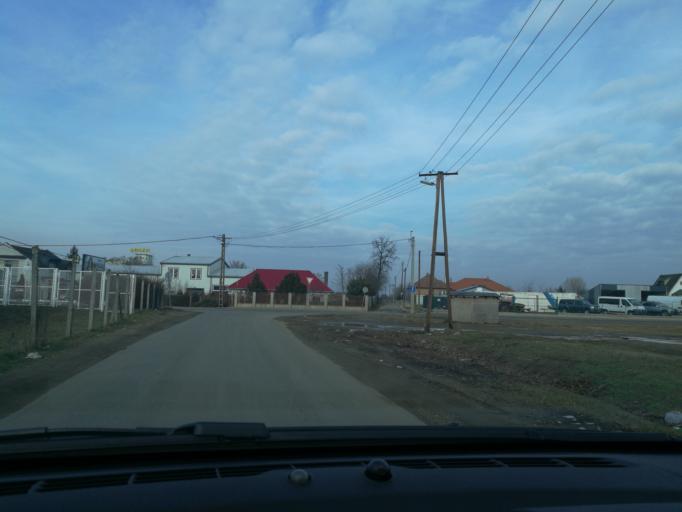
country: HU
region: Szabolcs-Szatmar-Bereg
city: Nyiregyhaza
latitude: 47.9329
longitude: 21.7344
